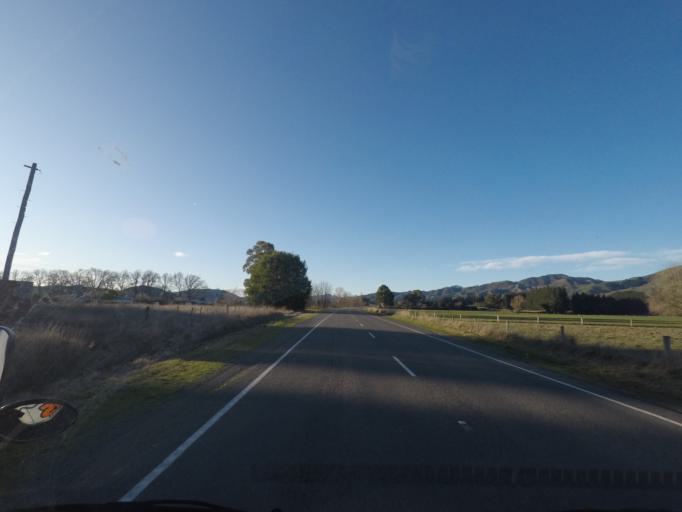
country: NZ
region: Canterbury
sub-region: Kaikoura District
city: Kaikoura
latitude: -42.7115
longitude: 173.2919
